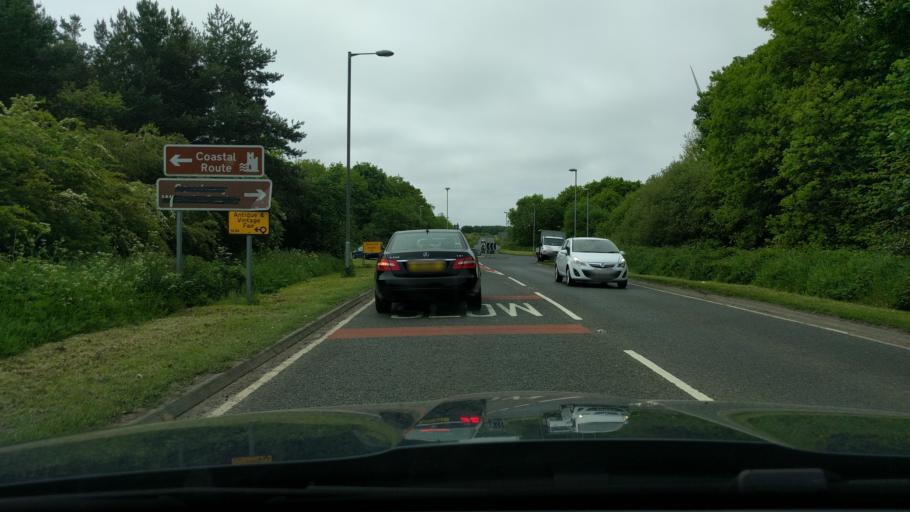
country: GB
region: England
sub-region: Northumberland
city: Cresswell
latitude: 55.2093
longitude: -1.5727
